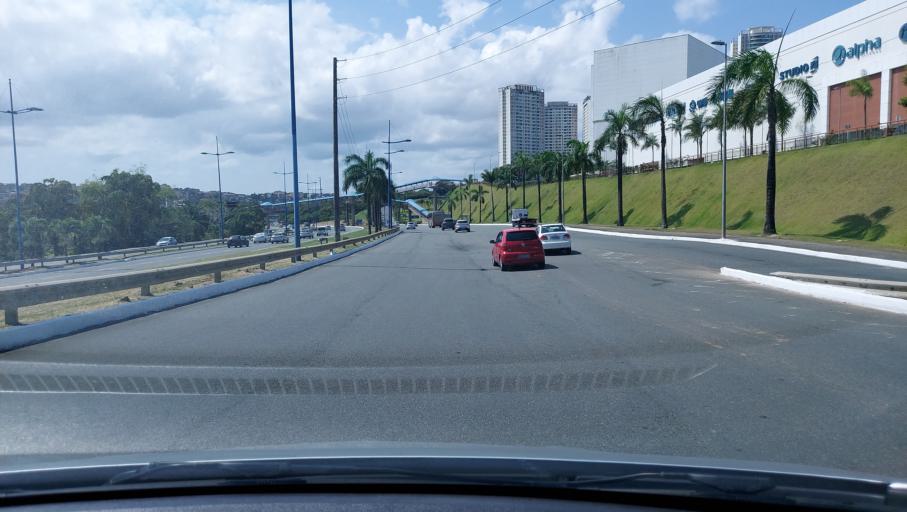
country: BR
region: Bahia
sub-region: Salvador
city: Salvador
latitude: -12.9720
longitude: -38.4753
